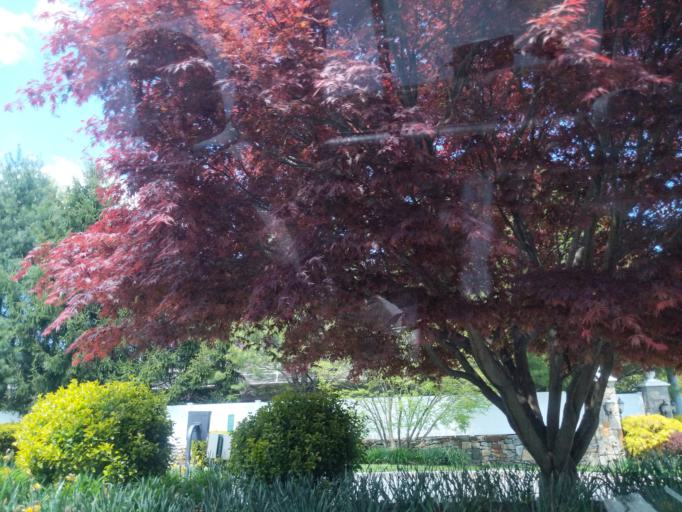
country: US
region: New York
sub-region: Westchester County
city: Tuckahoe
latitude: 40.9581
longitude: -73.7953
